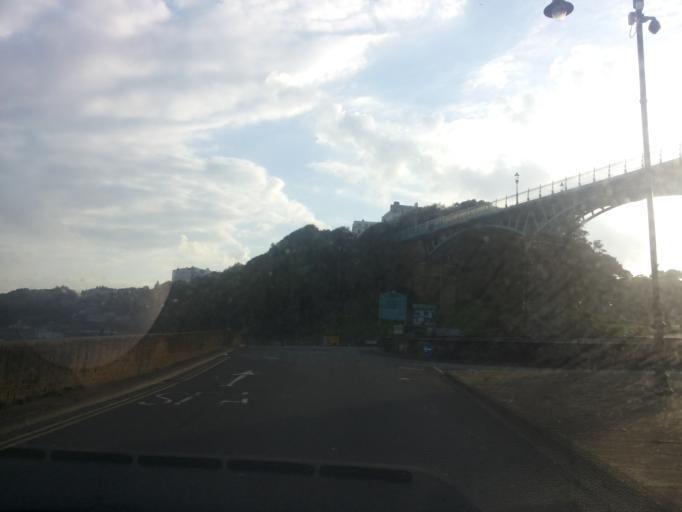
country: GB
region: England
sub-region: North Yorkshire
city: Scarborough
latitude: 54.2797
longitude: -0.3976
